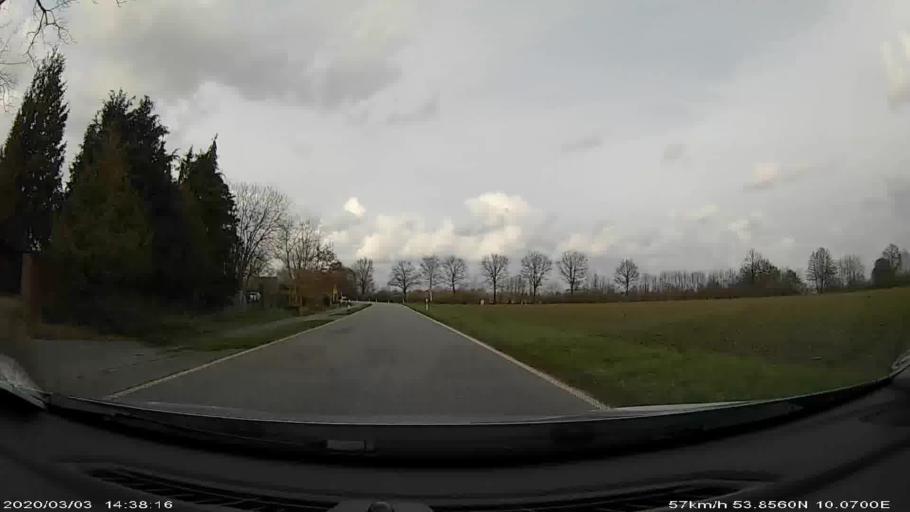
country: DE
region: Schleswig-Holstein
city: Struvenhutten
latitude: 53.8564
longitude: 10.0699
